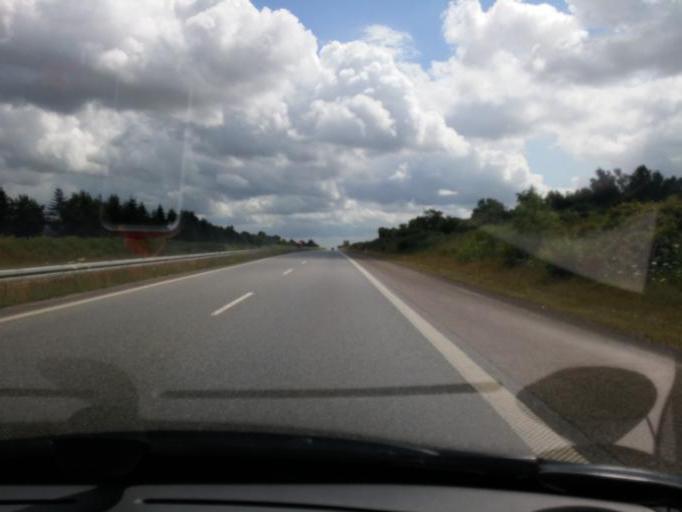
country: DK
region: South Denmark
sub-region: Faaborg-Midtfyn Kommune
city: Ringe
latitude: 55.2124
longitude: 10.5049
